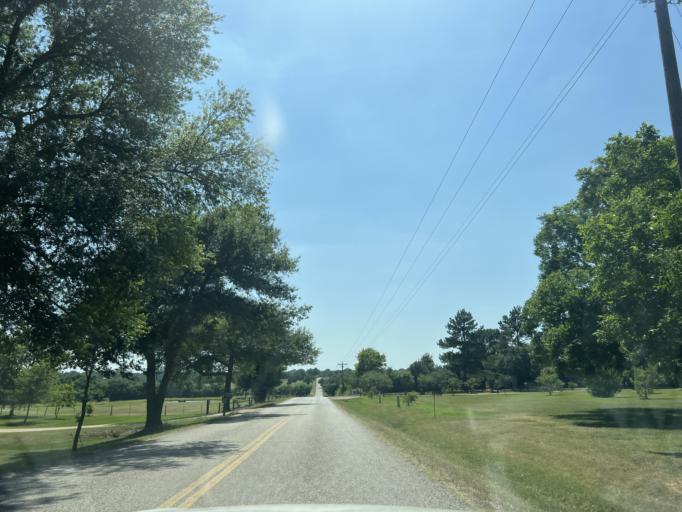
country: US
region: Texas
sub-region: Washington County
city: Brenham
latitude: 30.1610
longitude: -96.4348
